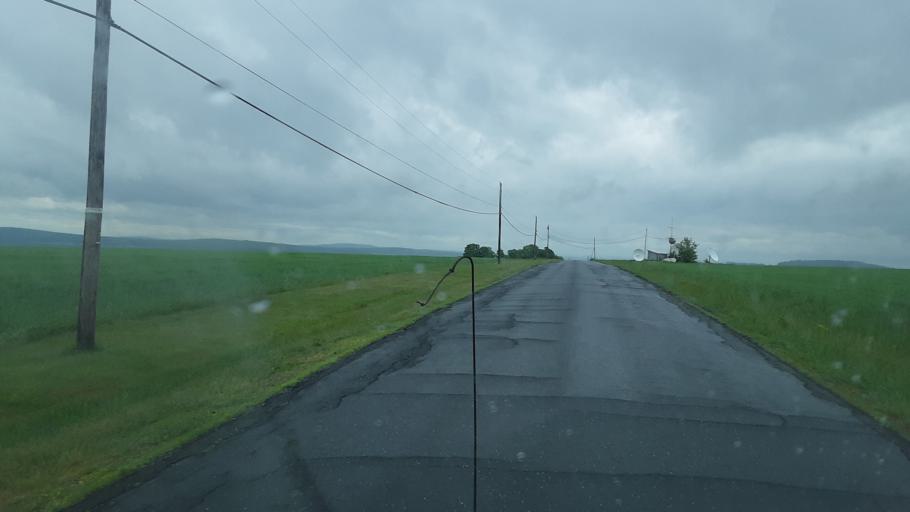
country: US
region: Maine
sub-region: Aroostook County
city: Presque Isle
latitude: 46.6818
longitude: -68.1870
